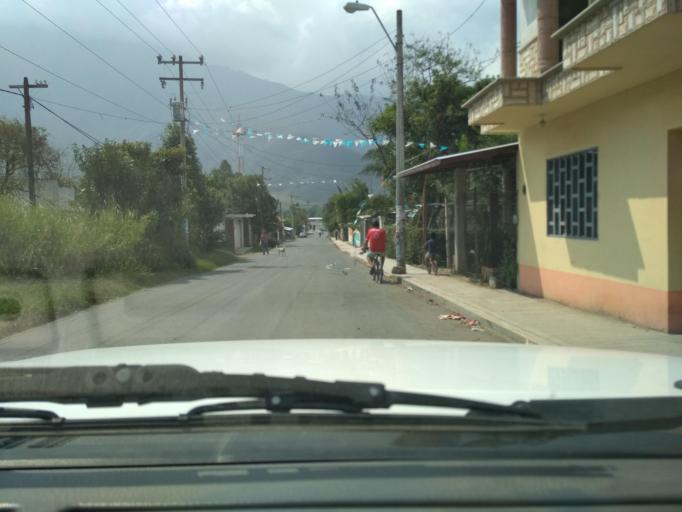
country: MX
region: Veracruz
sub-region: Acultzingo
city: Acatla
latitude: 18.7589
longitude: -97.2260
